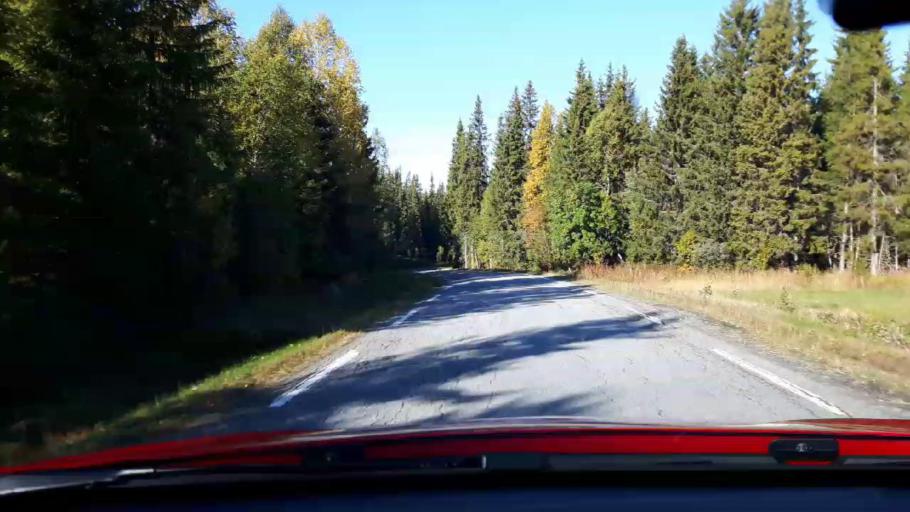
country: NO
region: Nord-Trondelag
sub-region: Lierne
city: Sandvika
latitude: 64.6241
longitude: 13.6896
